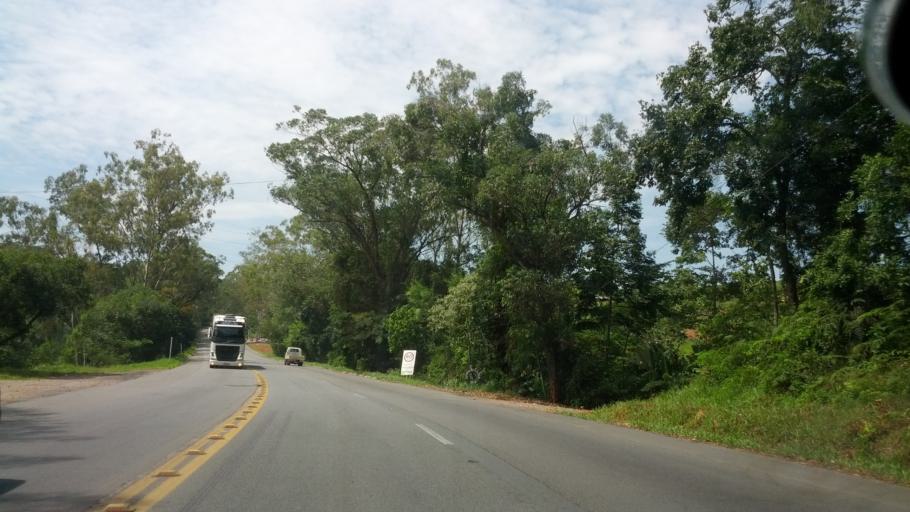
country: BR
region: Santa Catarina
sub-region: Ibirama
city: Ibirama
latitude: -27.0976
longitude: -49.5308
